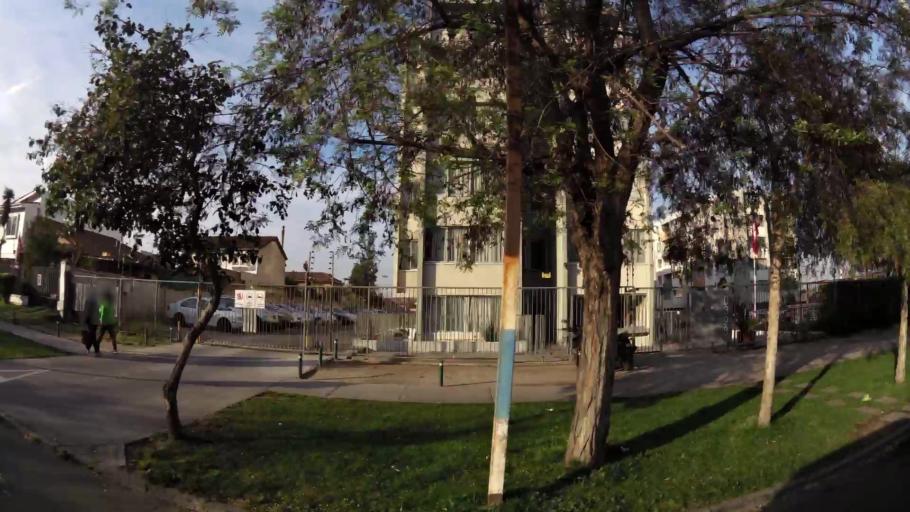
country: CL
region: Santiago Metropolitan
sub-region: Provincia de Santiago
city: La Pintana
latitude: -33.5336
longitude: -70.6690
